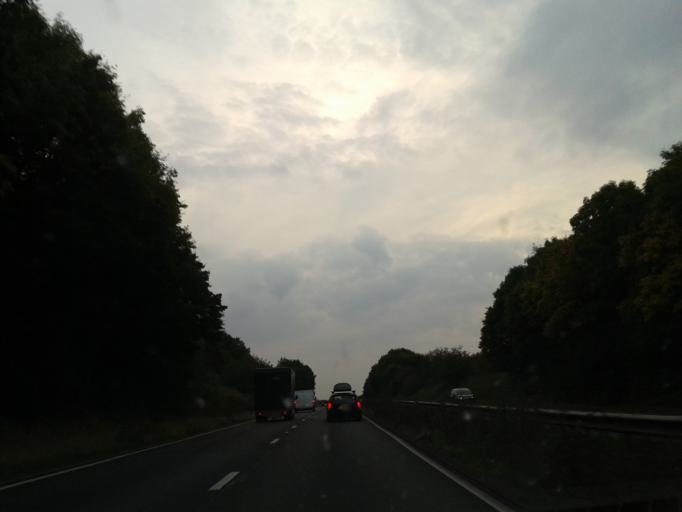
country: GB
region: England
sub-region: Warwickshire
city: Warwick
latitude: 52.2996
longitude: -1.5867
